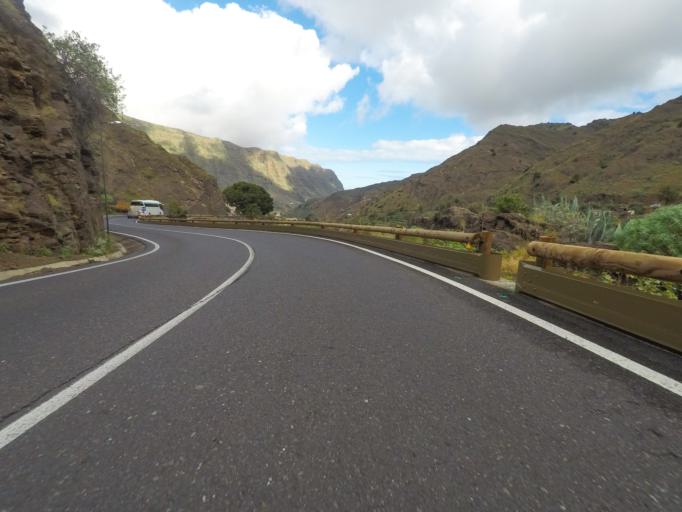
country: ES
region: Canary Islands
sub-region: Provincia de Santa Cruz de Tenerife
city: Hermigua
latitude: 28.1448
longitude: -17.1975
